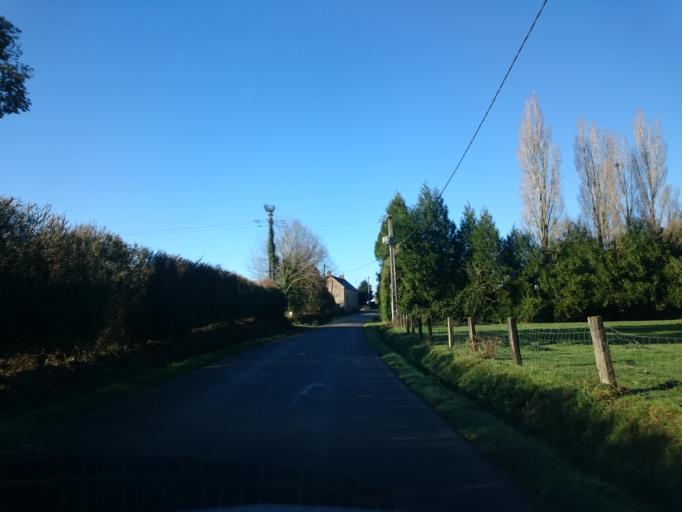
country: FR
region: Brittany
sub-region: Departement d'Ille-et-Vilaine
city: Corps-Nuds
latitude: 47.9514
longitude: -1.5497
